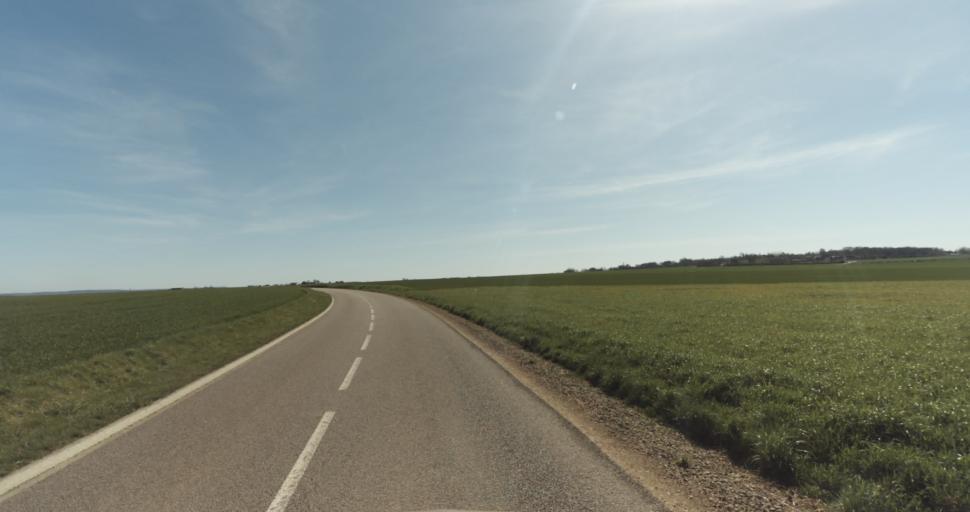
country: FR
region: Lower Normandy
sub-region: Departement du Calvados
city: Canon
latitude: 49.0428
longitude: -0.0679
